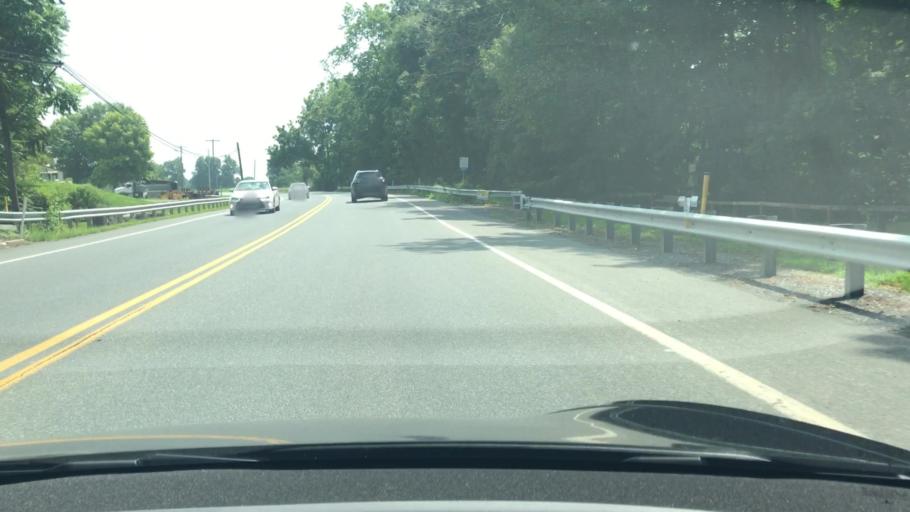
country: US
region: Pennsylvania
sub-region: Lancaster County
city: Salunga
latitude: 40.1071
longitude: -76.4482
